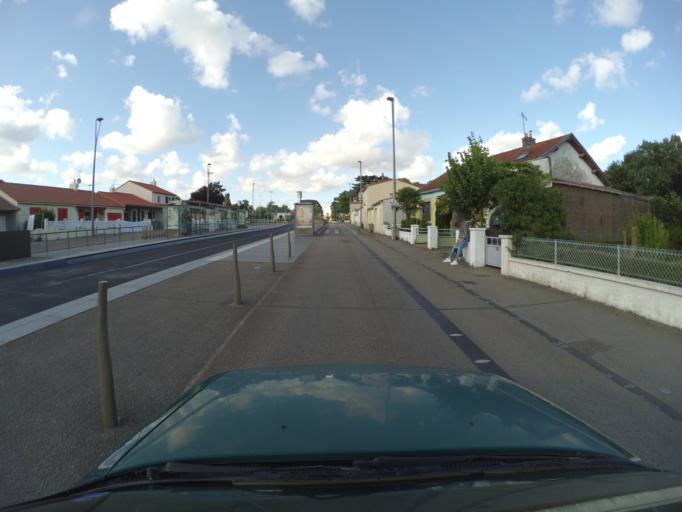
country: FR
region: Pays de la Loire
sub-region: Departement de la Loire-Atlantique
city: Saint-Sebastien-sur-Loire
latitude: 47.1871
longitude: -1.5211
